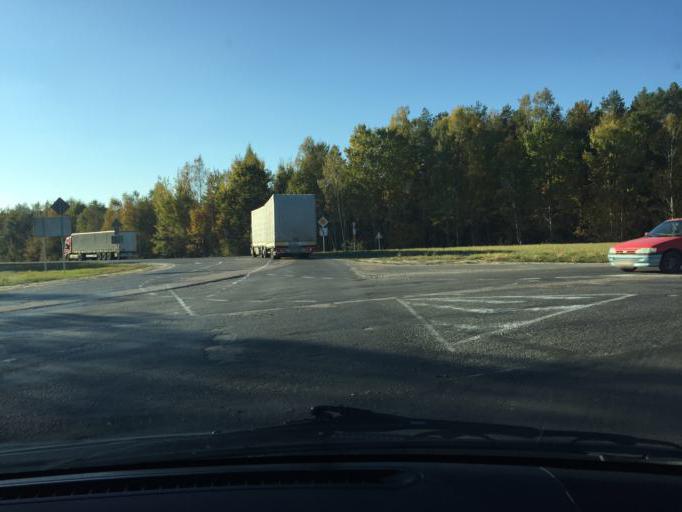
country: BY
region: Brest
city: Luninyets
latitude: 52.2828
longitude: 26.8261
